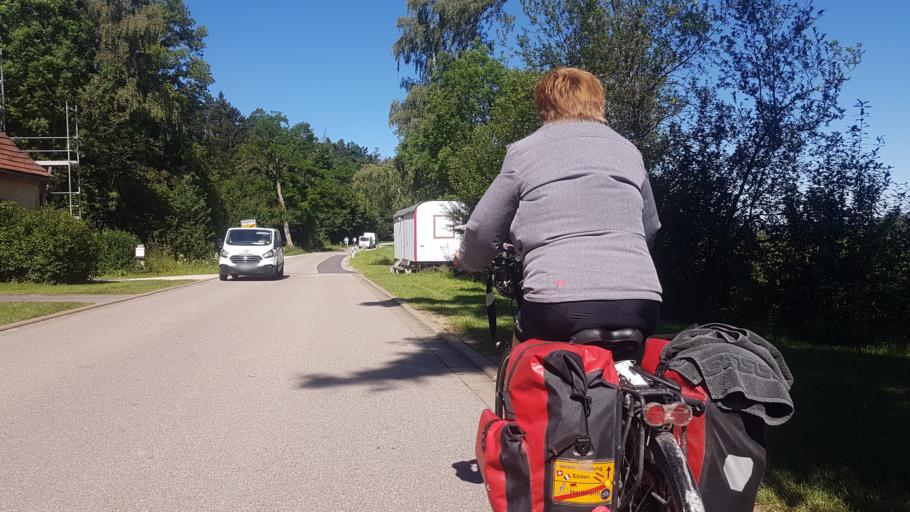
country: DE
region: Bavaria
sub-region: Regierungsbezirk Mittelfranken
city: Burgoberbach
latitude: 49.2057
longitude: 10.5469
